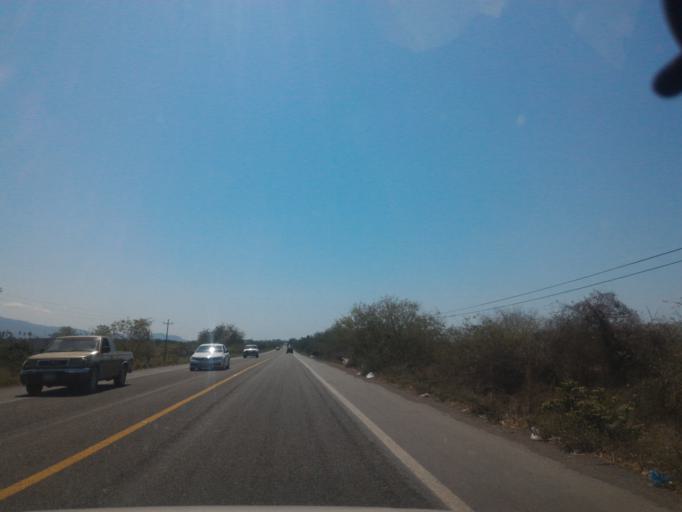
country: MX
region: Michoacan
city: Coahuayana Viejo
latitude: 18.7423
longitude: -103.7241
